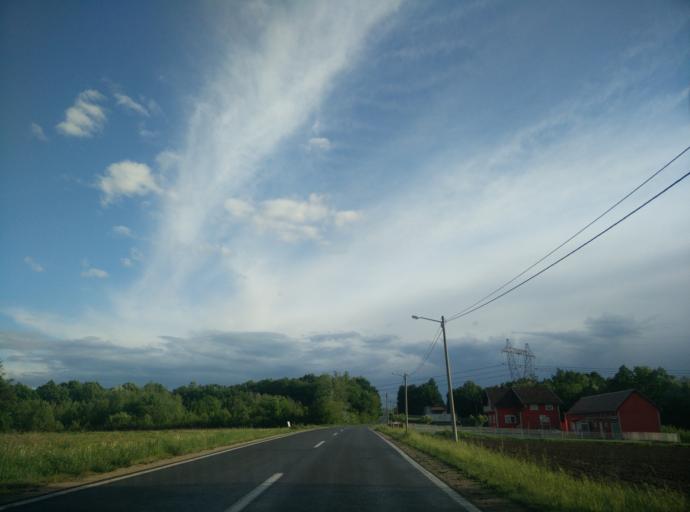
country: BA
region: Brcko
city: Brcko
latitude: 44.8074
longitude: 18.8100
